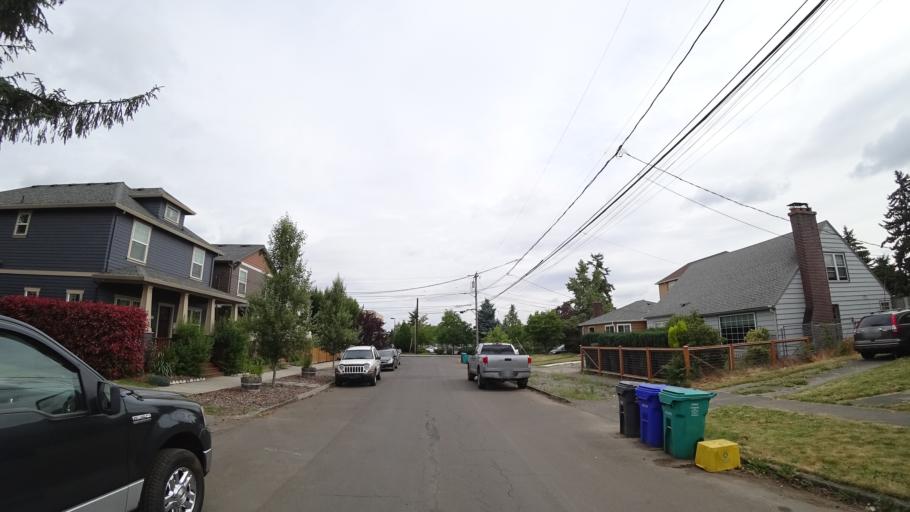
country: US
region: Oregon
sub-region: Multnomah County
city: Portland
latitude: 45.5748
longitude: -122.6798
